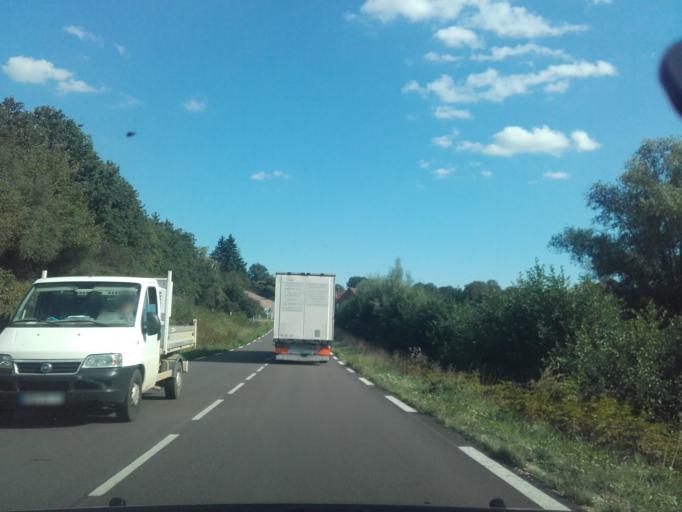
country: FR
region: Bourgogne
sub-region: Departement de Saone-et-Loire
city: Epinac
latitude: 46.9661
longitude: 4.5377
